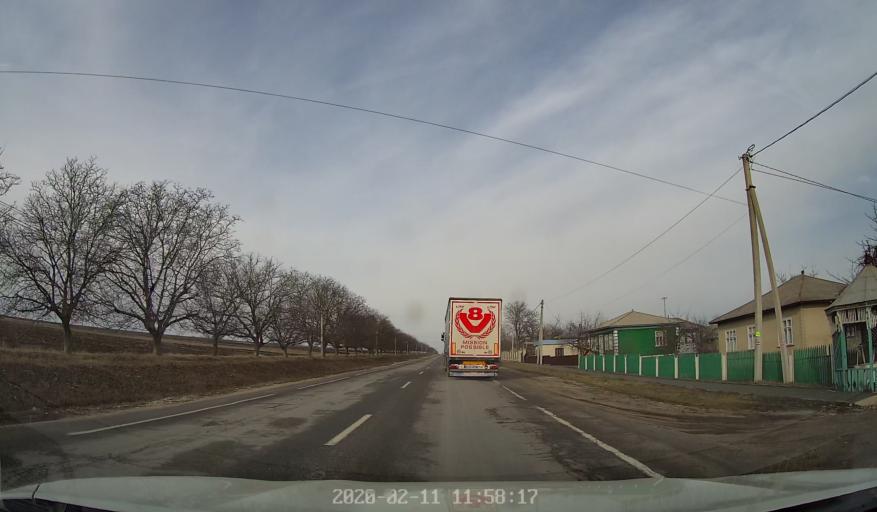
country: MD
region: Riscani
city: Riscani
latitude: 47.9025
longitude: 27.6664
